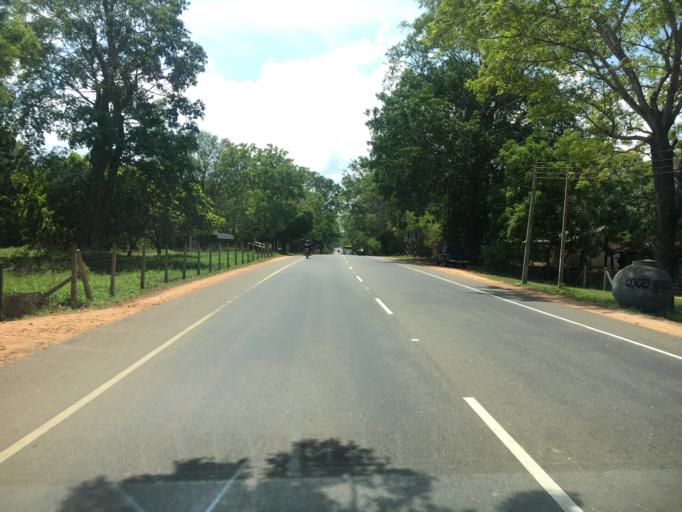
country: LK
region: North Central
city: Anuradhapura
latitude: 8.2668
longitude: 80.5048
